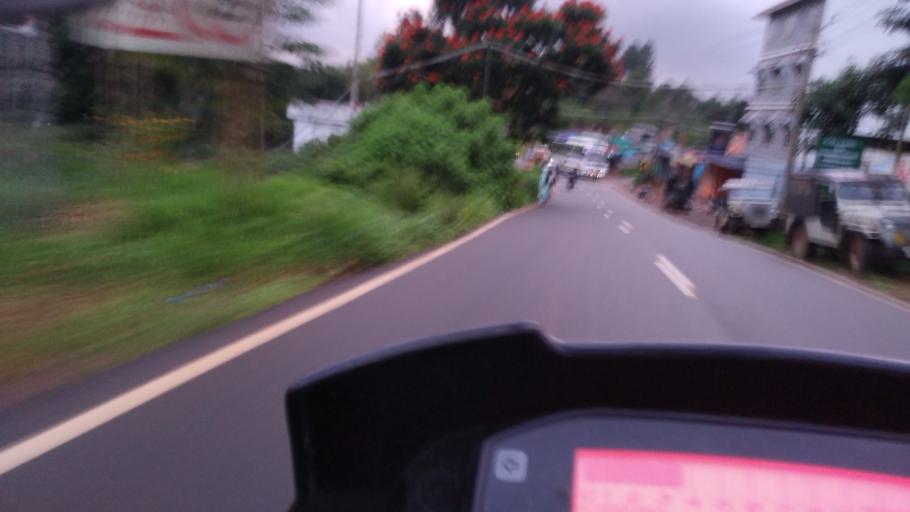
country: IN
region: Kerala
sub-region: Idukki
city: Munnar
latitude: 9.9651
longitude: 77.1017
